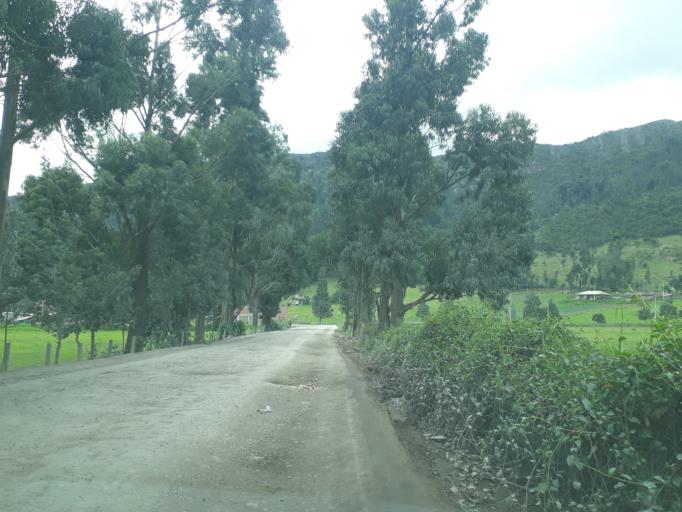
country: CO
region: Cundinamarca
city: Lenguazaque
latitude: 5.3292
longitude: -73.7081
